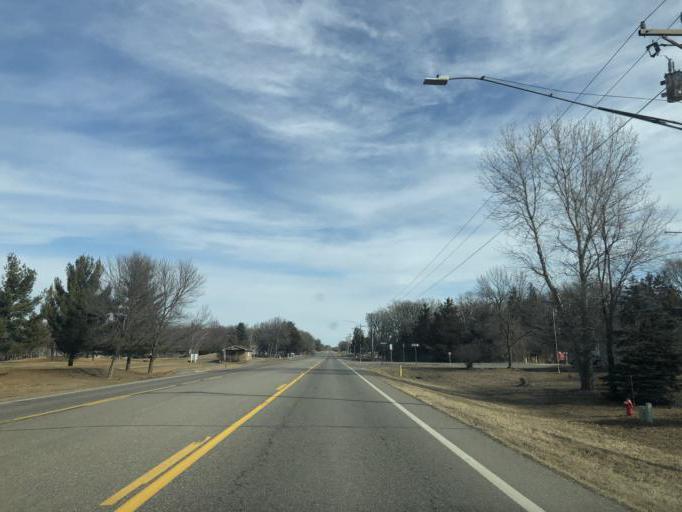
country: US
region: Minnesota
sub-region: Sherburne County
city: Becker
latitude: 45.4034
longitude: -93.8704
